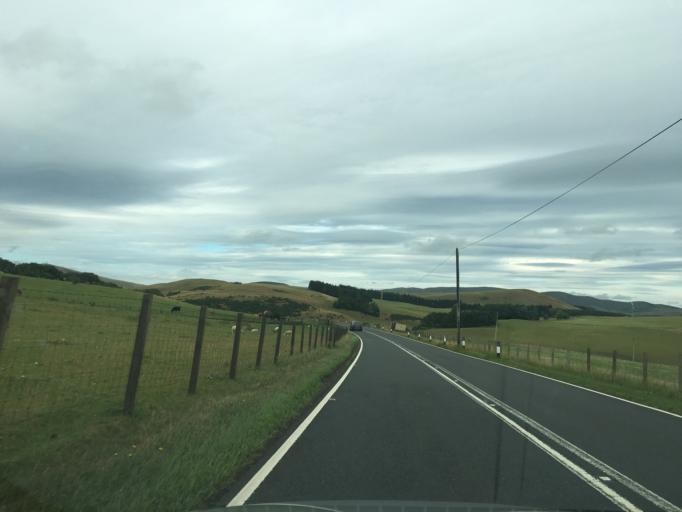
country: GB
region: Scotland
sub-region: South Lanarkshire
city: Biggar
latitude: 55.6432
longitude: -3.4929
